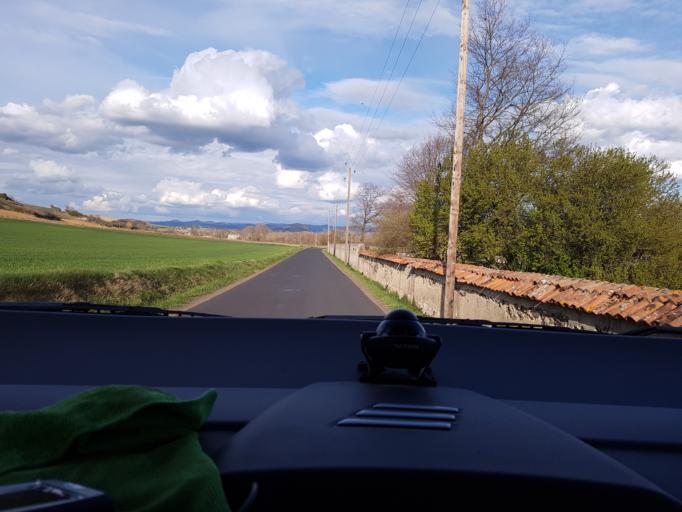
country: FR
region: Auvergne
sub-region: Departement du Puy-de-Dome
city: Saint-Germain-Lembron
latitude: 45.4532
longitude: 3.2091
